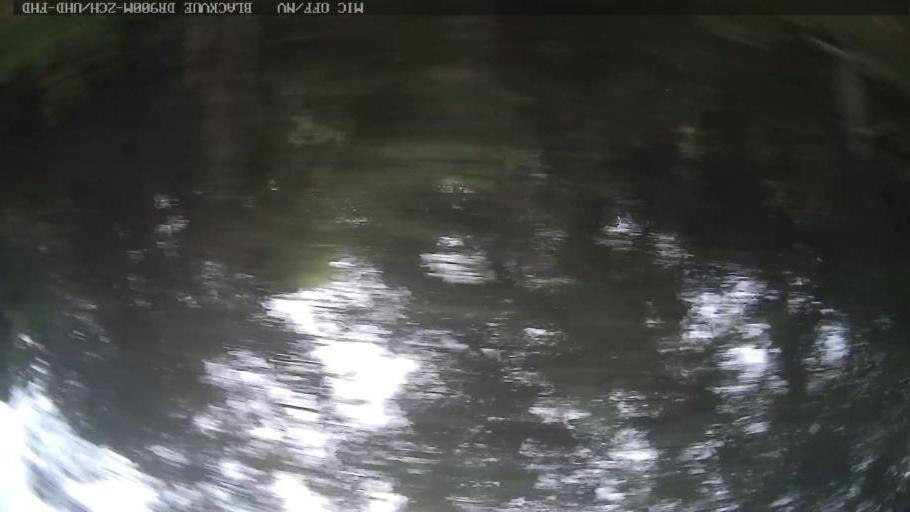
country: BR
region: Sao Paulo
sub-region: Rio Grande Da Serra
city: Rio Grande da Serra
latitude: -23.6925
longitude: -46.3052
